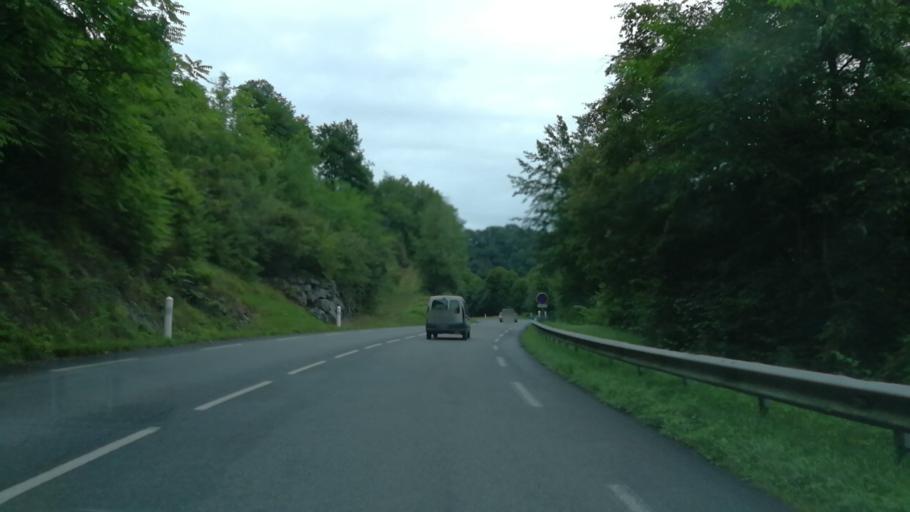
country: FR
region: Aquitaine
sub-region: Departement des Pyrenees-Atlantiques
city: Arette
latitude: 43.0996
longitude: -0.6224
